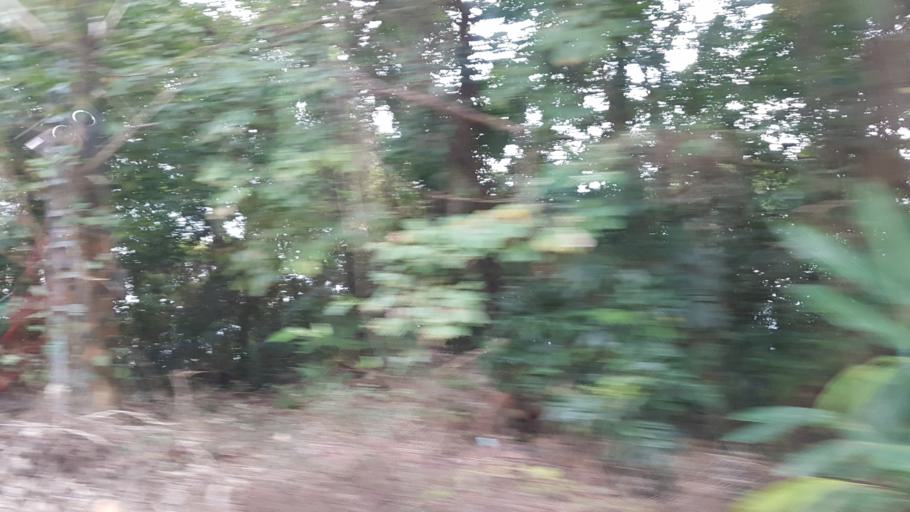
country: TW
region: Taiwan
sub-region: Chiayi
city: Jiayi Shi
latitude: 23.3215
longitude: 120.4829
